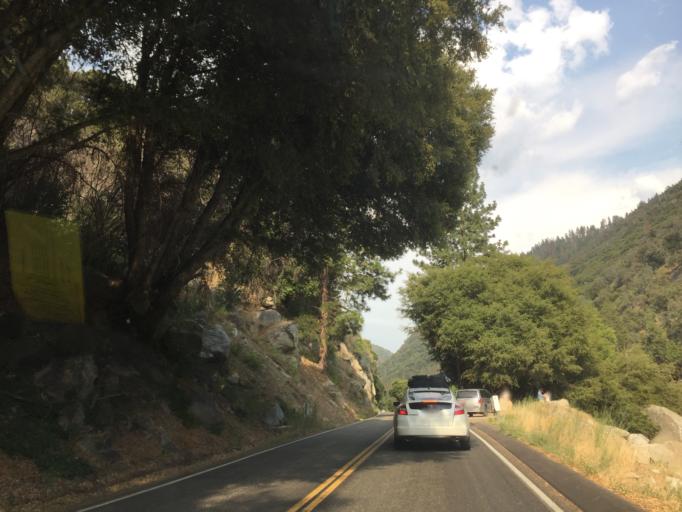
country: US
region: California
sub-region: Tulare County
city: Three Rivers
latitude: 36.8089
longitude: -118.7764
